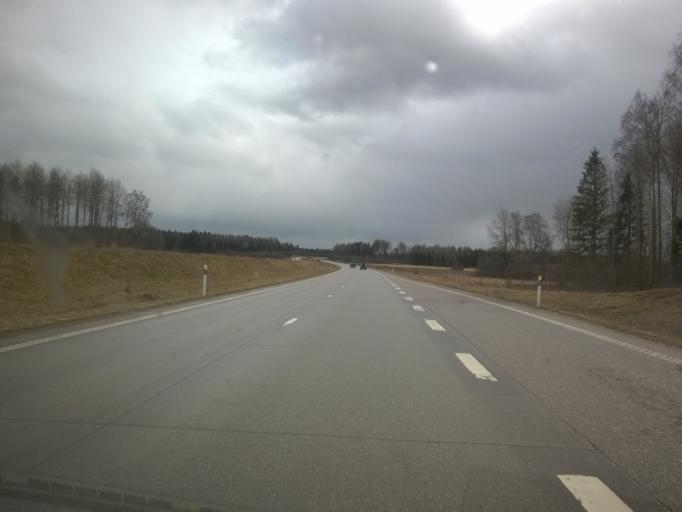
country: SE
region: Uppsala
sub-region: Osthammars Kommun
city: Bjorklinge
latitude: 60.0064
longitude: 17.6268
